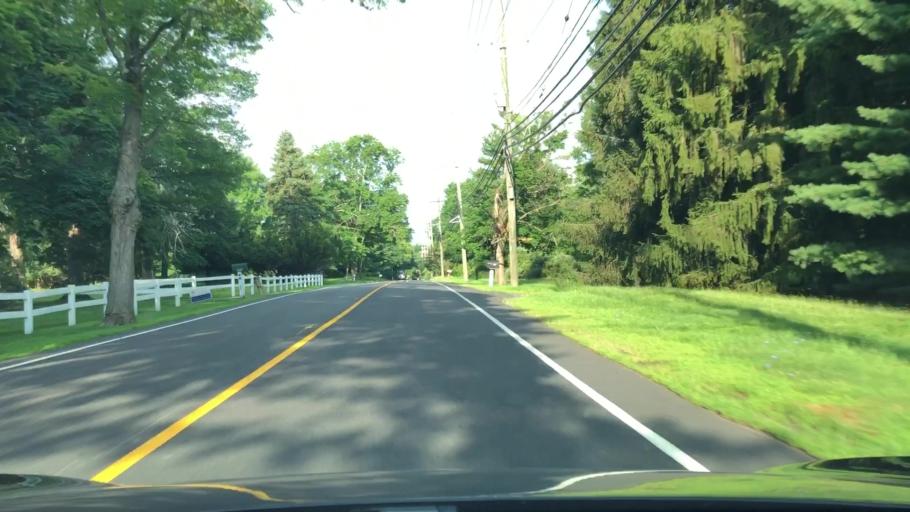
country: US
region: New Jersey
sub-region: Mercer County
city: Lawrenceville
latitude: 40.3396
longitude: -74.7162
